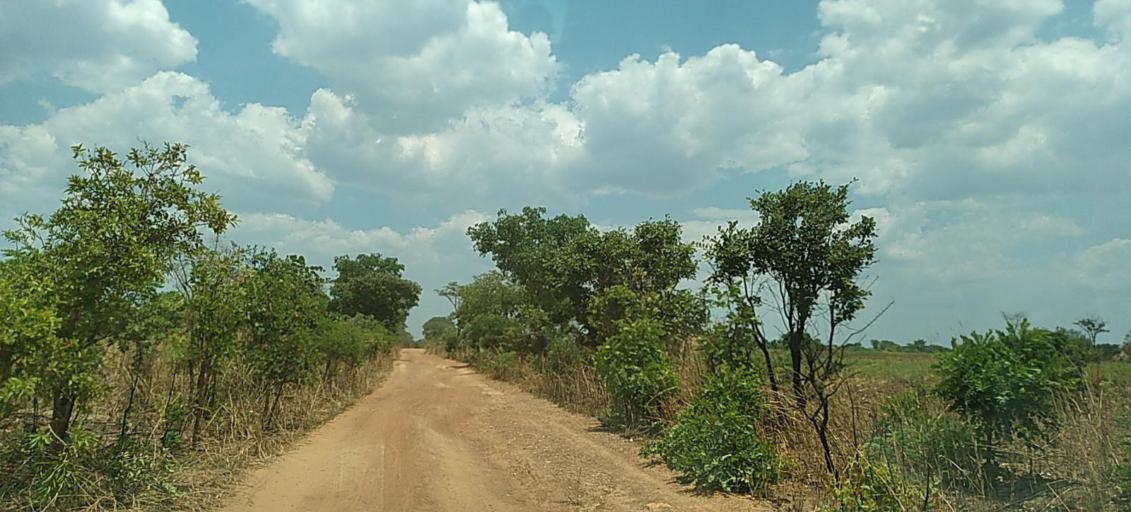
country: ZM
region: Copperbelt
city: Luanshya
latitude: -13.3757
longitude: 28.4273
